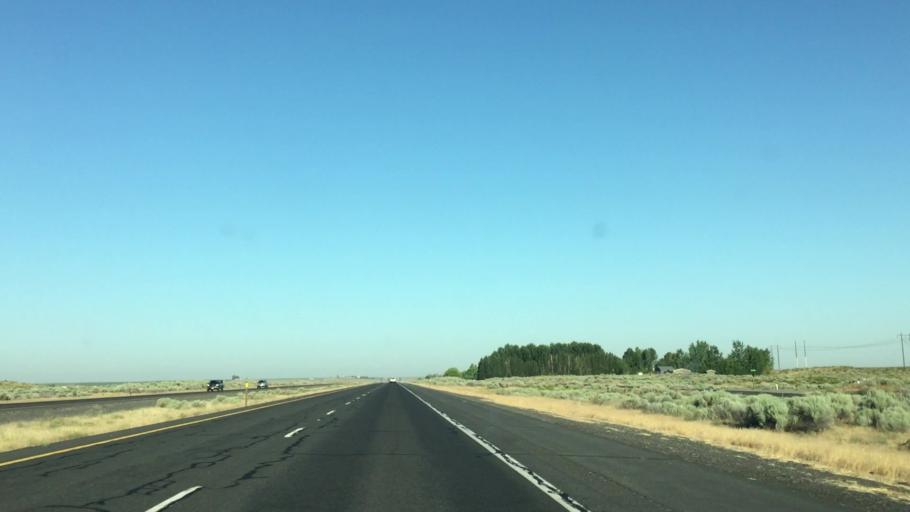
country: US
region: Washington
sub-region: Grant County
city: Cascade Valley
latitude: 47.1042
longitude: -119.4052
